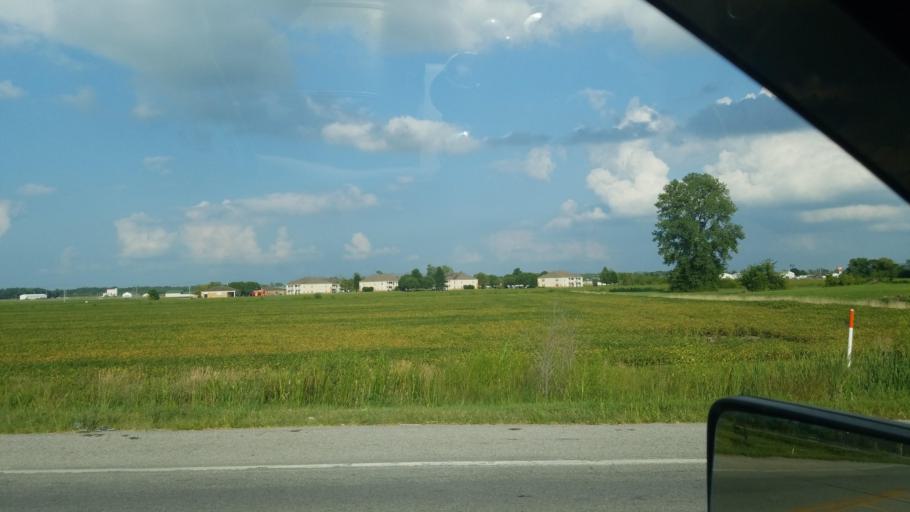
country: US
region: Illinois
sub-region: Saline County
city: Harrisburg
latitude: 37.7497
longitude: -88.5393
